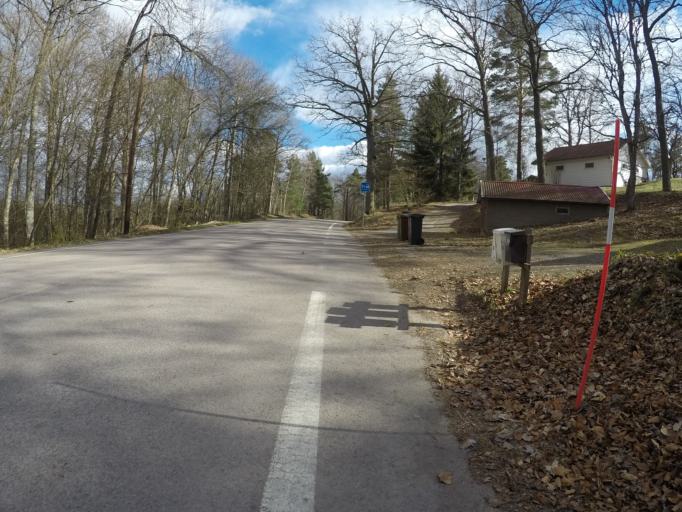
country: SE
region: Soedermanland
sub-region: Eskilstuna Kommun
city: Kvicksund
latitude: 59.4775
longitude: 16.2874
